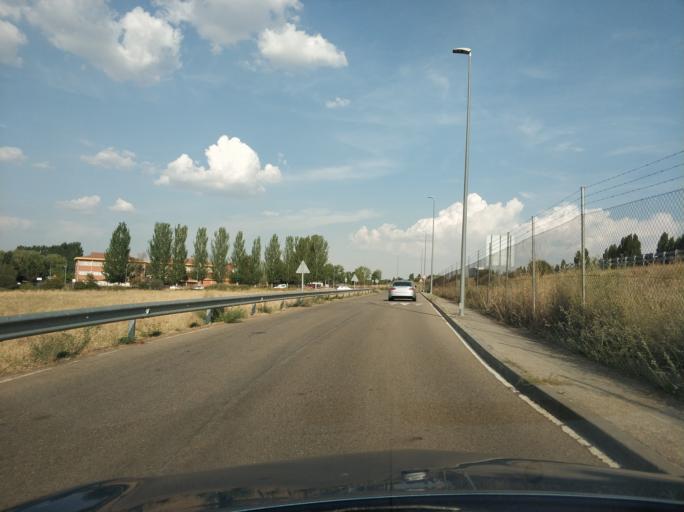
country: ES
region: Castille and Leon
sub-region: Provincia de Salamanca
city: Santa Marta de Tormes
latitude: 40.9449
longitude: -5.6288
